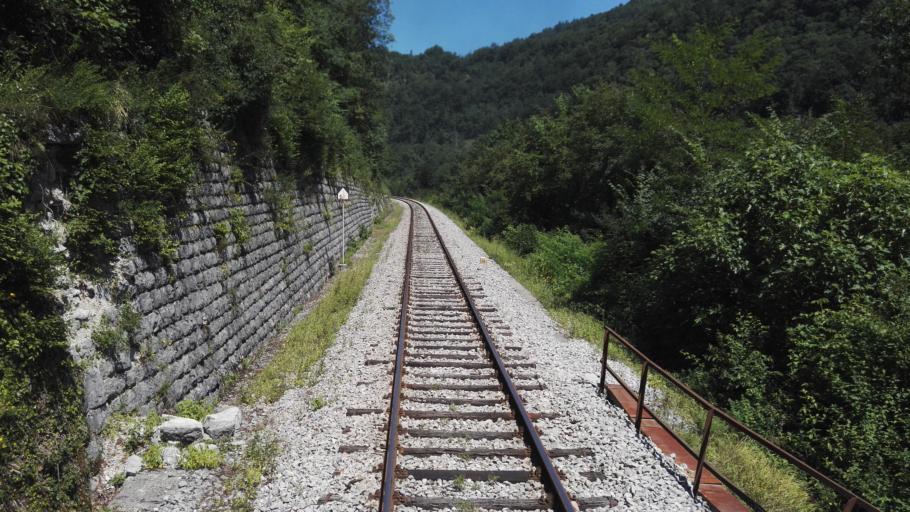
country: SI
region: Kanal
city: Deskle
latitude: 46.0221
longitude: 13.6057
